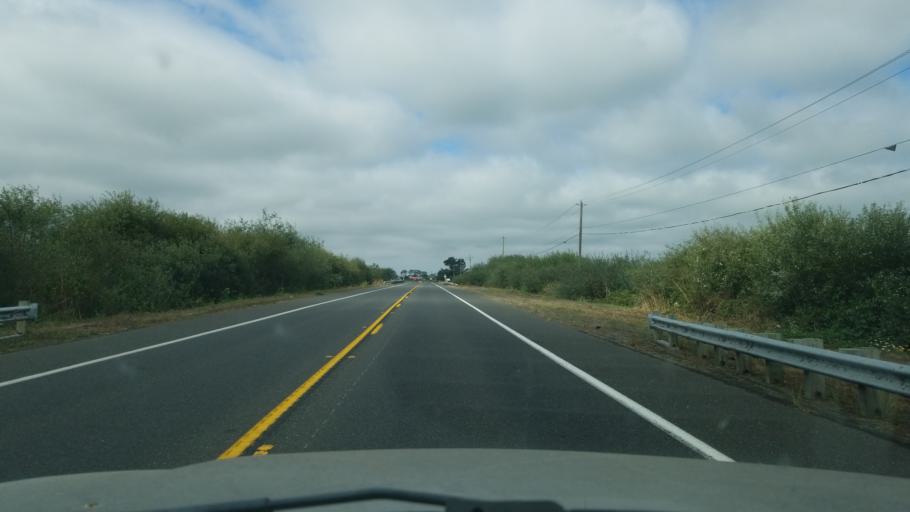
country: US
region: California
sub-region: Humboldt County
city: Ferndale
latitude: 40.5988
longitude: -124.2182
